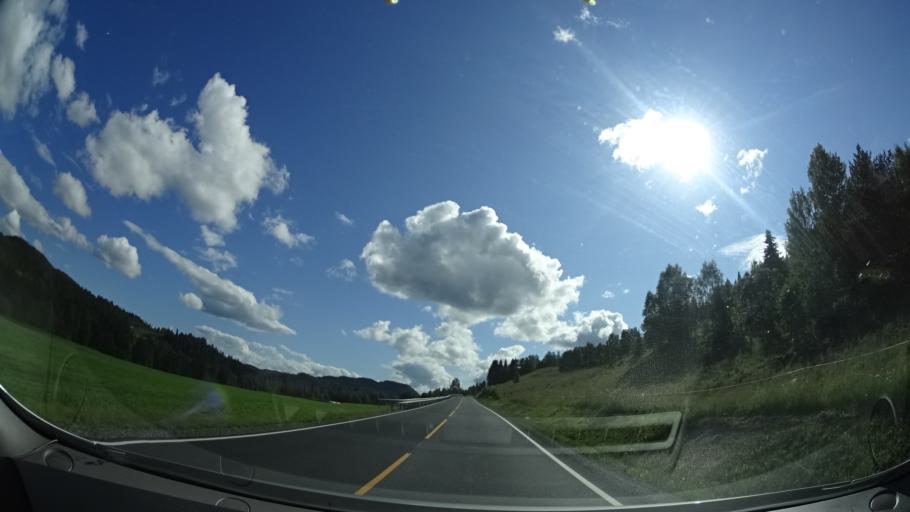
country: NO
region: Sor-Trondelag
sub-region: Snillfjord
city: Krokstadora
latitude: 63.2446
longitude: 9.5996
